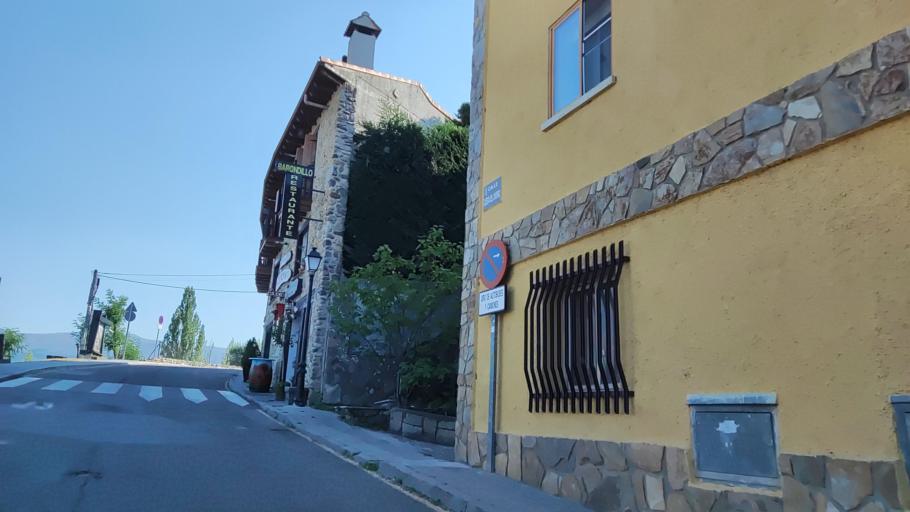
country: ES
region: Madrid
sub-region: Provincia de Madrid
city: Rascafria
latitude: 40.9021
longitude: -3.8785
